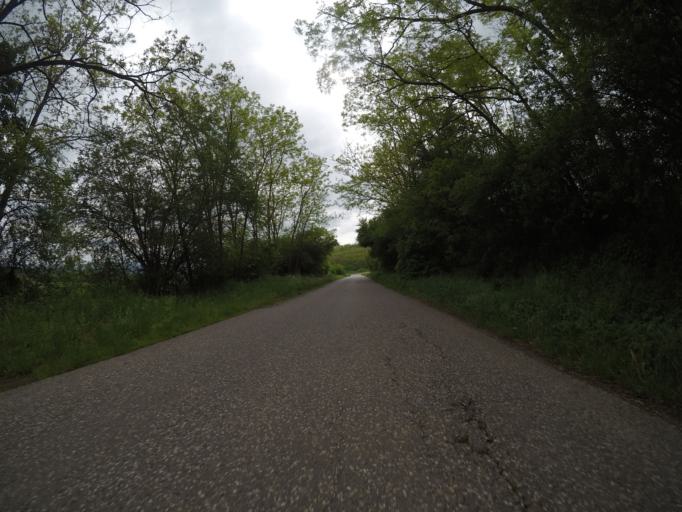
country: SK
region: Nitriansky
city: Sahy
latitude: 48.0903
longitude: 18.8689
